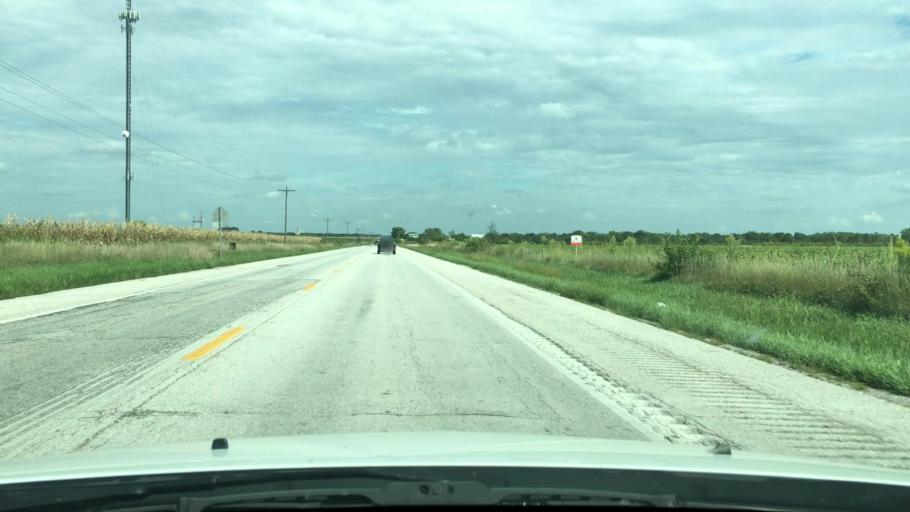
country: US
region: Missouri
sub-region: Montgomery County
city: Wellsville
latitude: 39.1681
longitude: -91.6478
